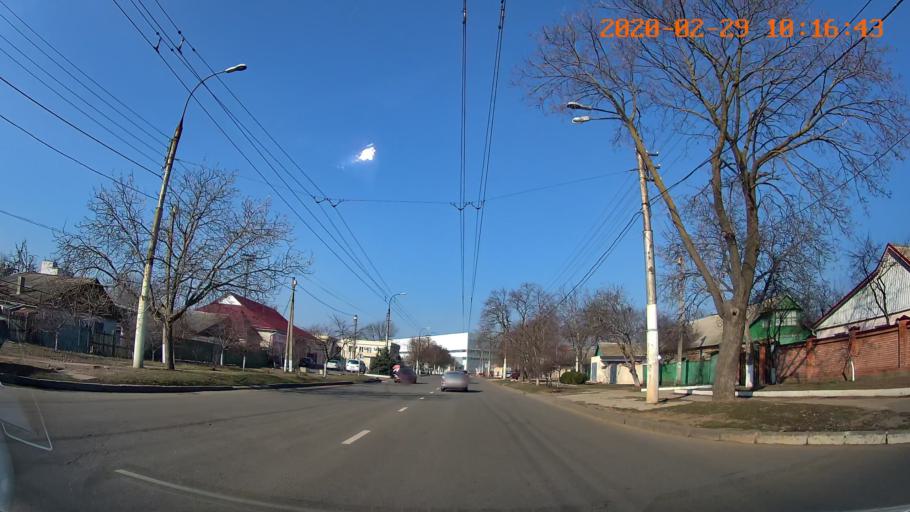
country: MD
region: Telenesti
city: Tiraspolul Nou
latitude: 46.8557
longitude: 29.6262
